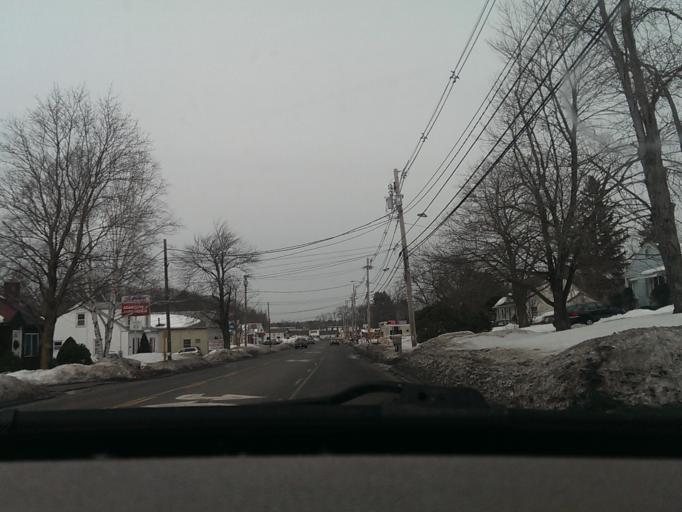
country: US
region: Massachusetts
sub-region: Hampden County
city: East Longmeadow
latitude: 42.0554
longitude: -72.5182
